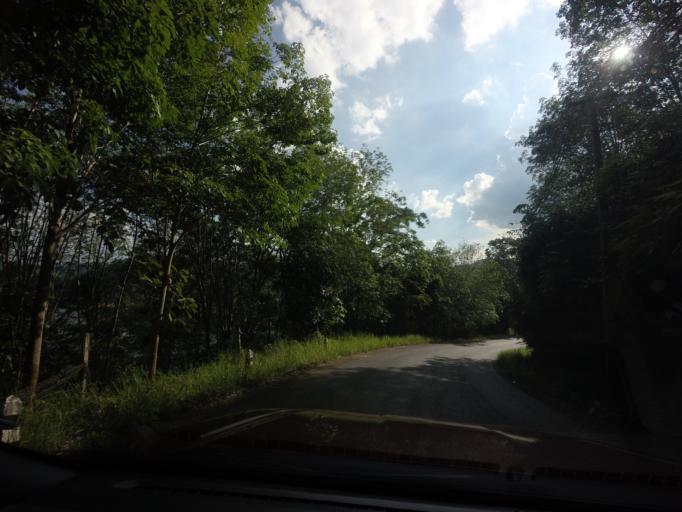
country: TH
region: Yala
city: Than To
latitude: 6.1361
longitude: 101.2923
